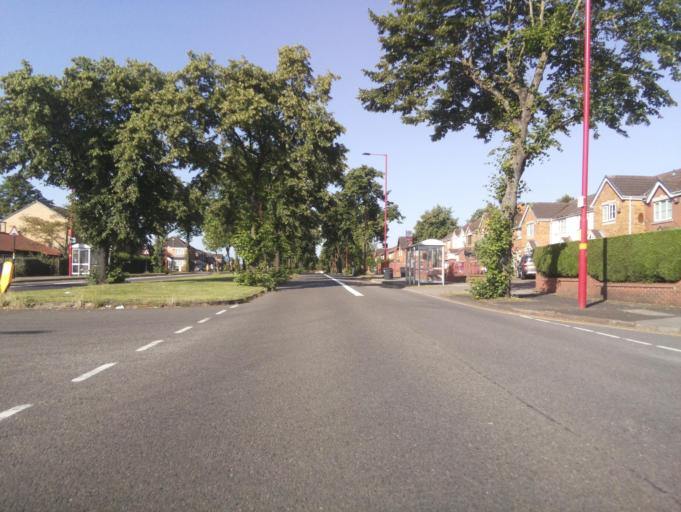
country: GB
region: England
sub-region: City and Borough of Birmingham
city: Sutton Coldfield
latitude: 52.5192
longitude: -1.8142
